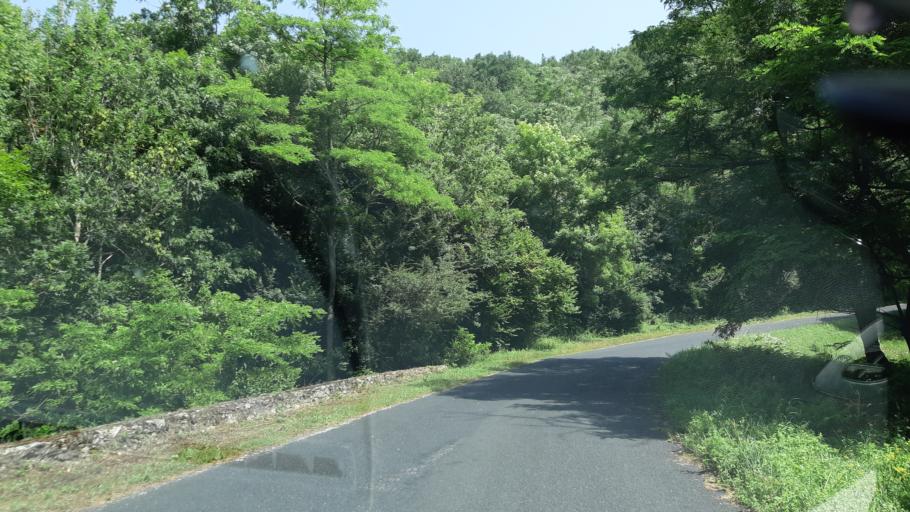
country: FR
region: Languedoc-Roussillon
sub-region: Departement des Pyrenees-Orientales
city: Arles
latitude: 42.5234
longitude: 2.6117
